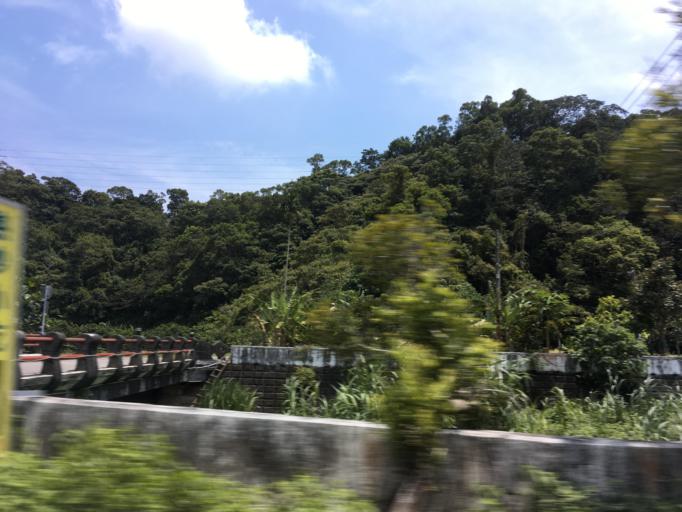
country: TW
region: Taiwan
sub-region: Yilan
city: Yilan
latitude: 24.8163
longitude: 121.7455
